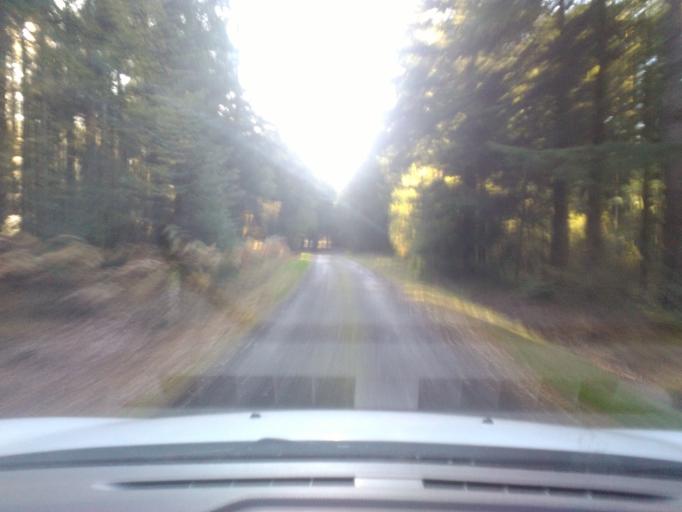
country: FR
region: Lorraine
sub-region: Departement des Vosges
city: Bruyeres
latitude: 48.2866
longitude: 6.7724
